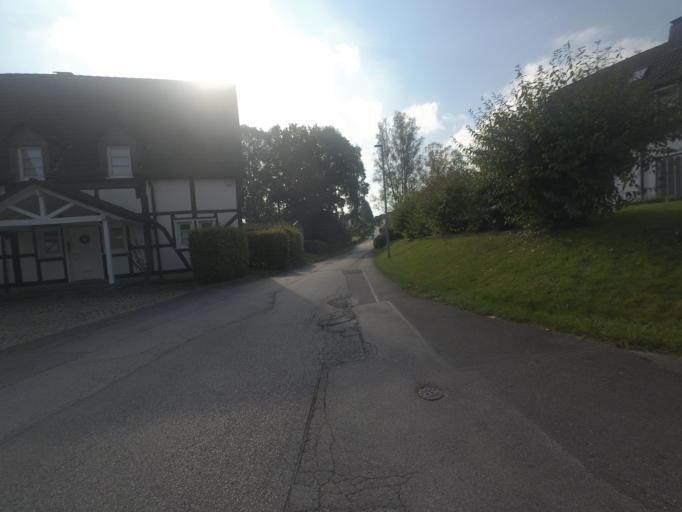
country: DE
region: North Rhine-Westphalia
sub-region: Regierungsbezirk Arnsberg
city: Frondenberg
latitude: 51.4598
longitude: 7.7280
